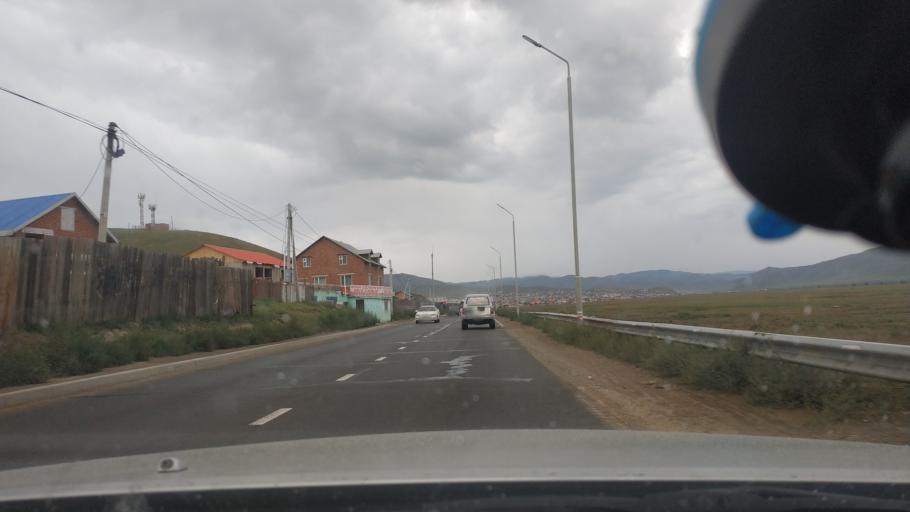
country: MN
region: Ulaanbaatar
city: Ulaanbaatar
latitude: 47.9133
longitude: 107.0473
